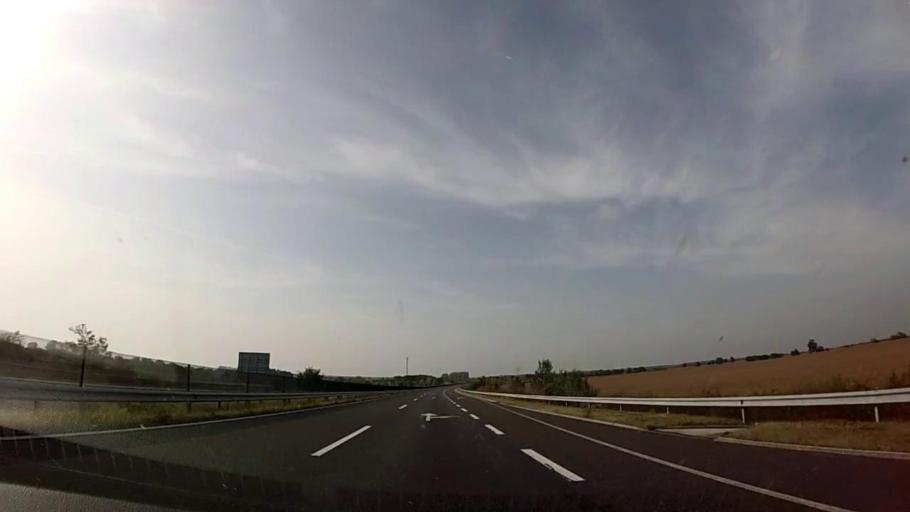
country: HU
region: Somogy
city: Balatonbereny
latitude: 46.6537
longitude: 17.3062
